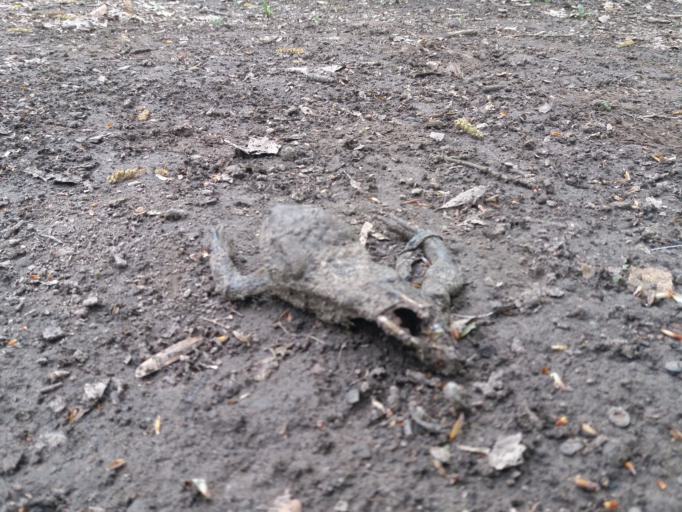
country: HU
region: Komarom-Esztergom
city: Labatlan
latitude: 47.6852
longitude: 18.5143
